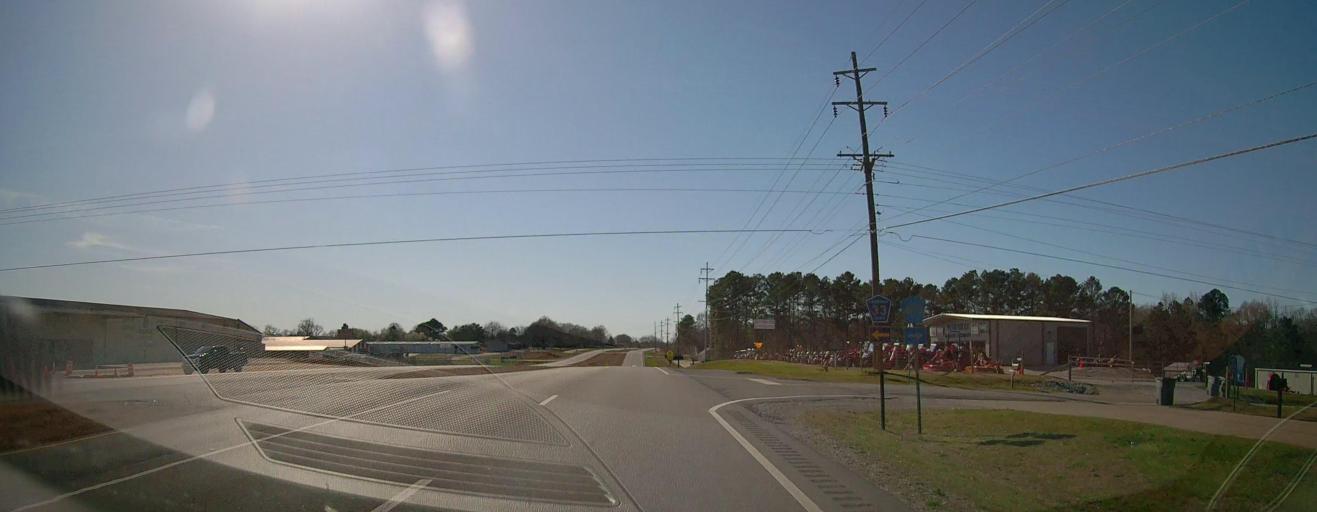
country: US
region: Alabama
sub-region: Lauderdale County
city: Killen
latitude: 34.8601
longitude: -87.4339
